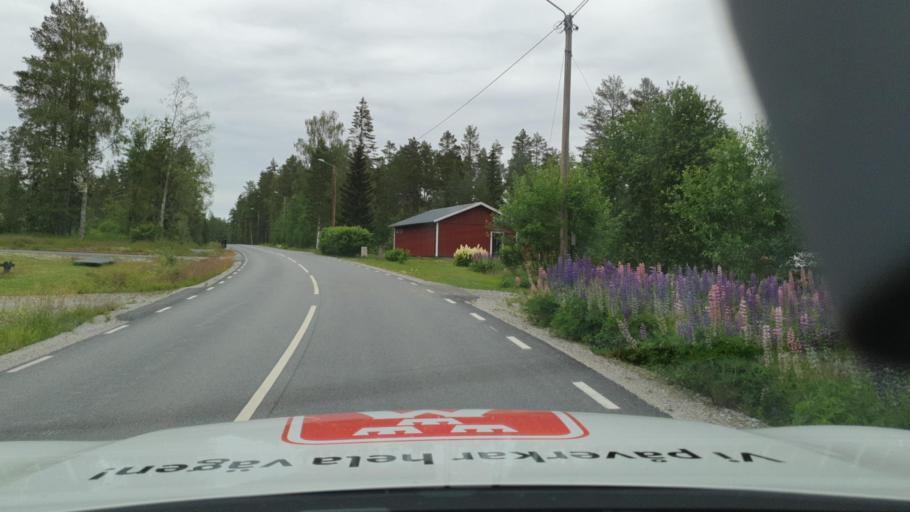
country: SE
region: Vaesterbotten
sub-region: Nordmalings Kommun
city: Nordmaling
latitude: 63.5025
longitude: 19.3294
